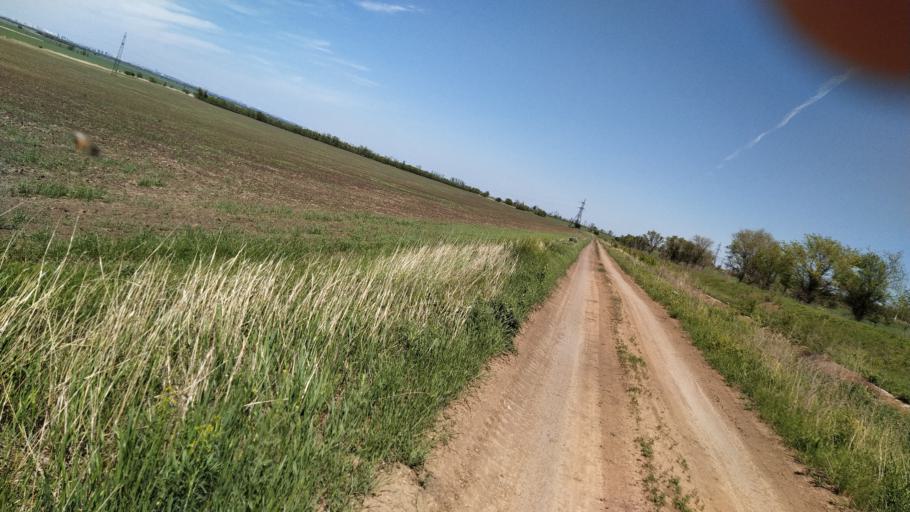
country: RU
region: Rostov
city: Kuleshovka
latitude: 47.0350
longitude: 39.6377
